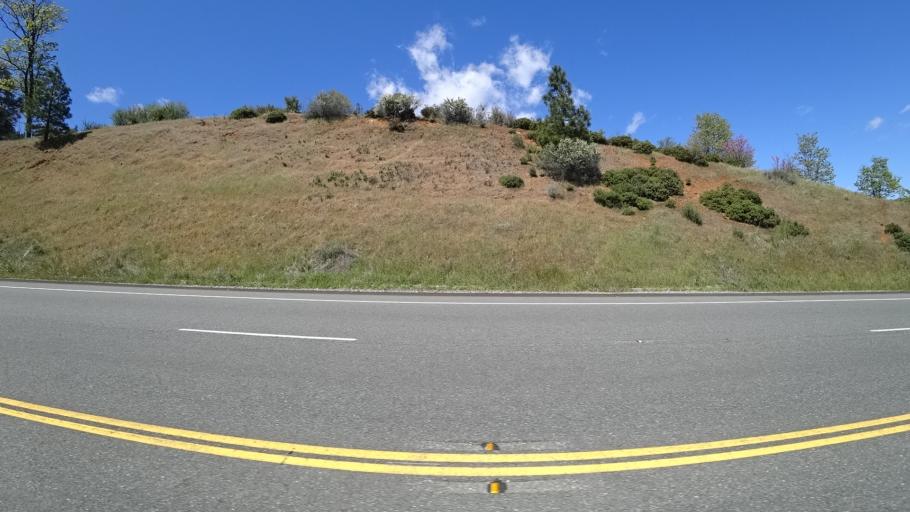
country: US
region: California
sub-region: Trinity County
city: Weaverville
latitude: 40.7465
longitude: -122.9725
